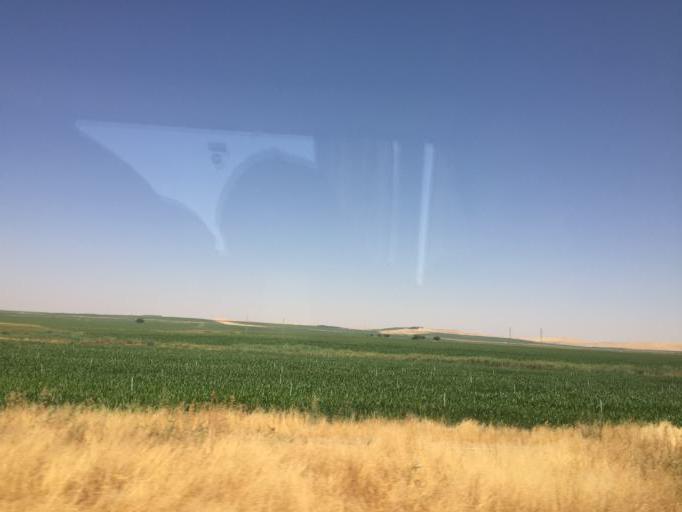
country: TR
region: Diyarbakir
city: Tepe
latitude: 37.8507
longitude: 40.7690
